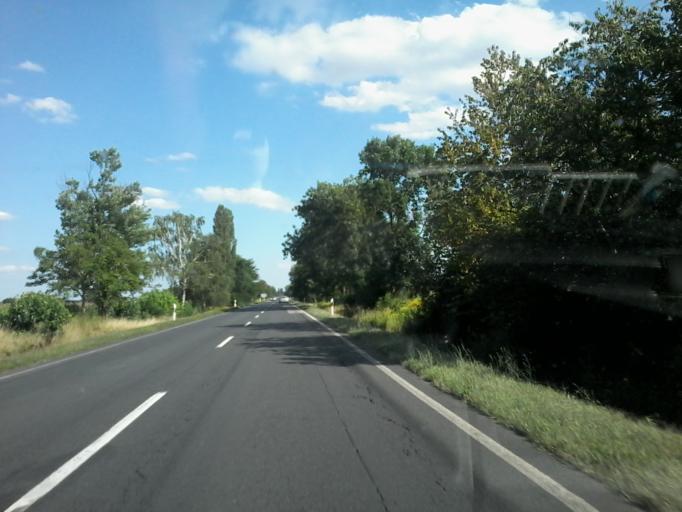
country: HU
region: Vas
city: Janoshaza
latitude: 47.1342
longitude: 17.1073
